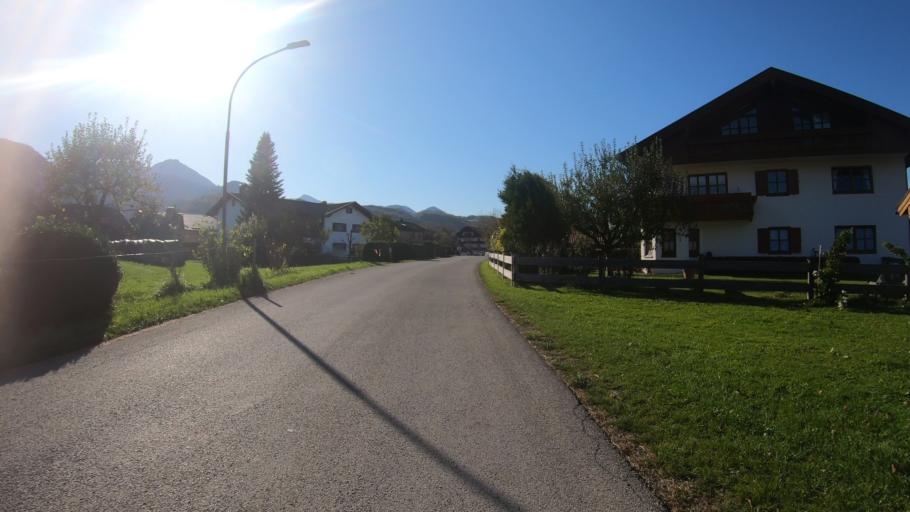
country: DE
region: Bavaria
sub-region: Upper Bavaria
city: Bergen
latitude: 47.8037
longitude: 12.5932
